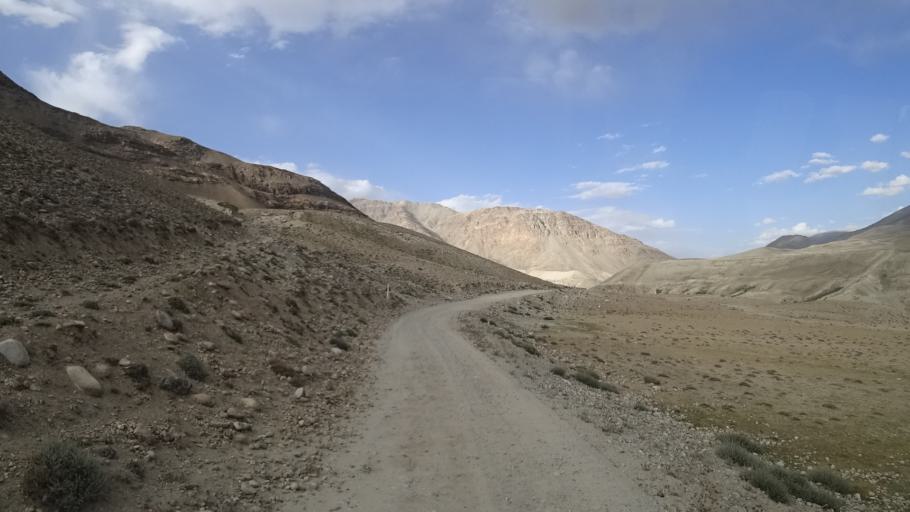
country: AF
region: Badakhshan
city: Khandud
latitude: 37.2223
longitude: 72.7944
